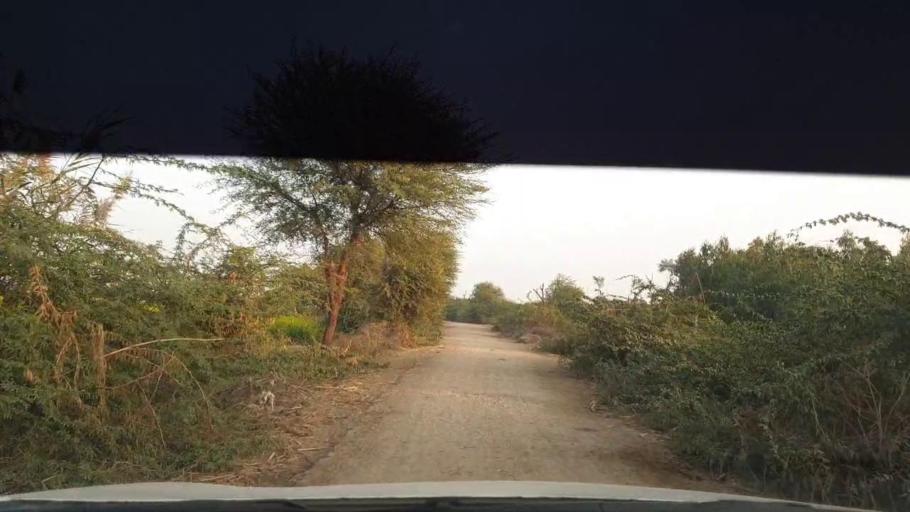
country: PK
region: Sindh
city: Berani
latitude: 25.7581
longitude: 68.9949
